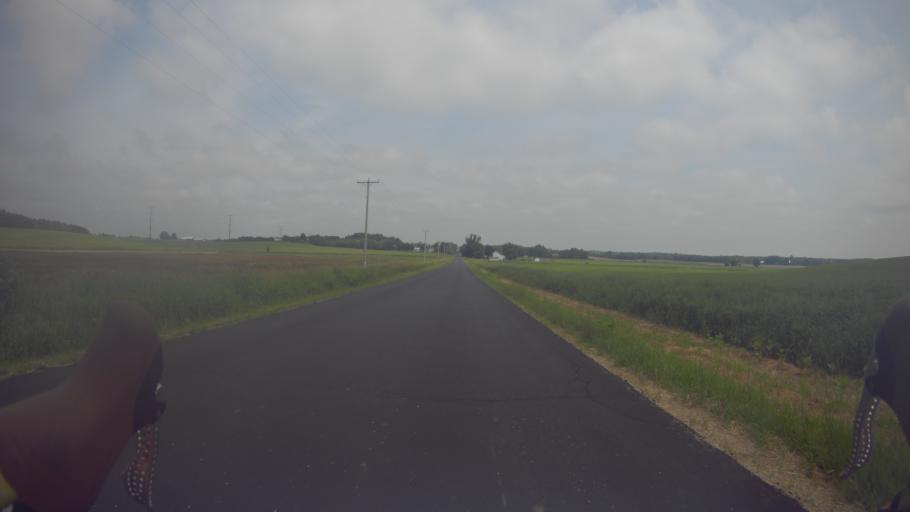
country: US
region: Wisconsin
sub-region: Rock County
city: Edgerton
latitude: 42.9133
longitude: -89.0427
